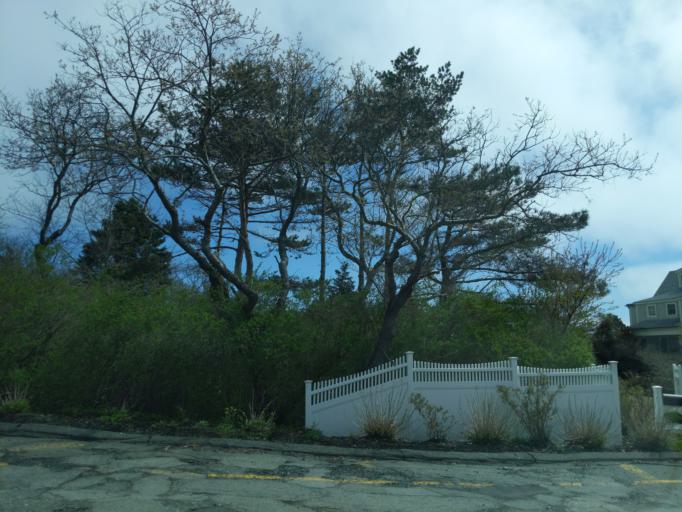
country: US
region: Massachusetts
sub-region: Essex County
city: Rockport
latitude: 42.6361
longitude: -70.6035
